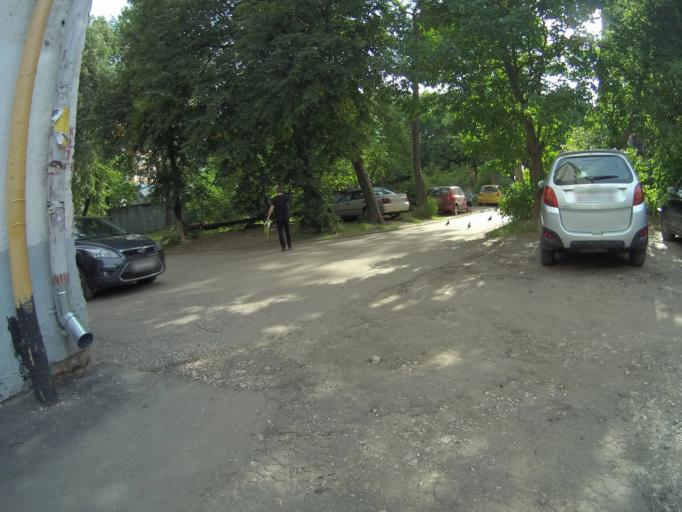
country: RU
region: Vladimir
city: Kommunar
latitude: 56.1471
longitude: 40.4338
